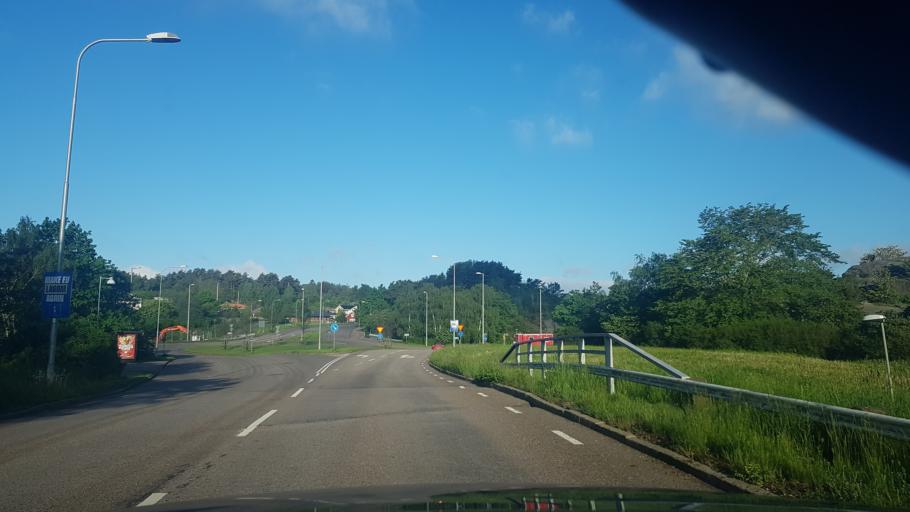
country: SE
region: Vaestra Goetaland
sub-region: Goteborg
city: Majorna
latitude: 57.6346
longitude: 11.8917
